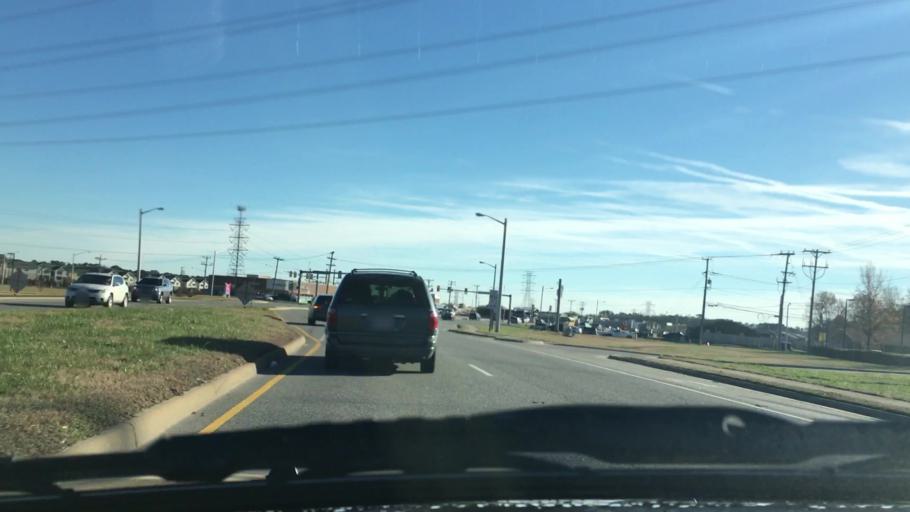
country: US
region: Virginia
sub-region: City of Portsmouth
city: Portsmouth Heights
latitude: 36.8791
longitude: -76.4241
